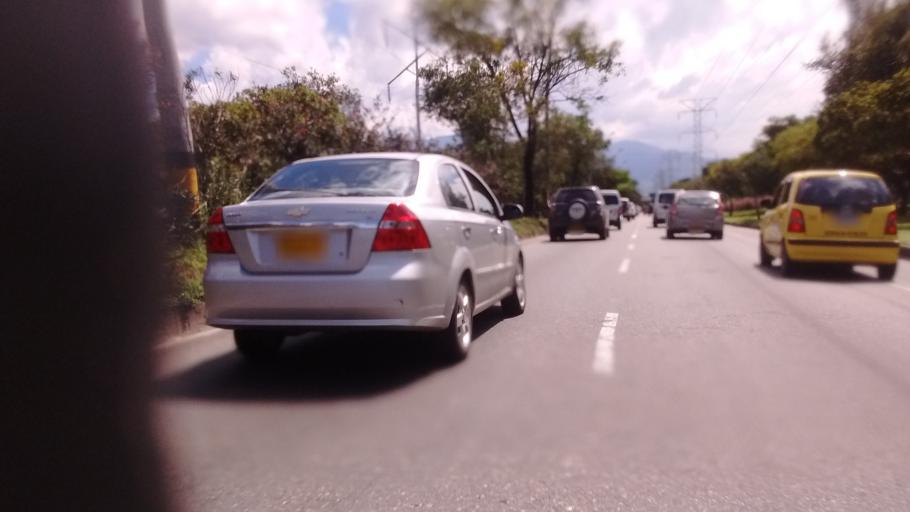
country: CO
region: Antioquia
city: Medellin
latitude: 6.2194
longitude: -75.5777
